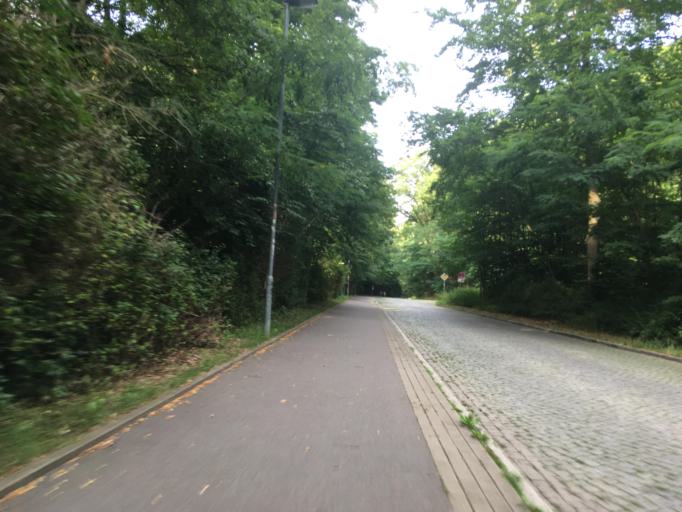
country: DE
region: Brandenburg
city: Eberswalde
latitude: 52.8236
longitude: 13.8253
